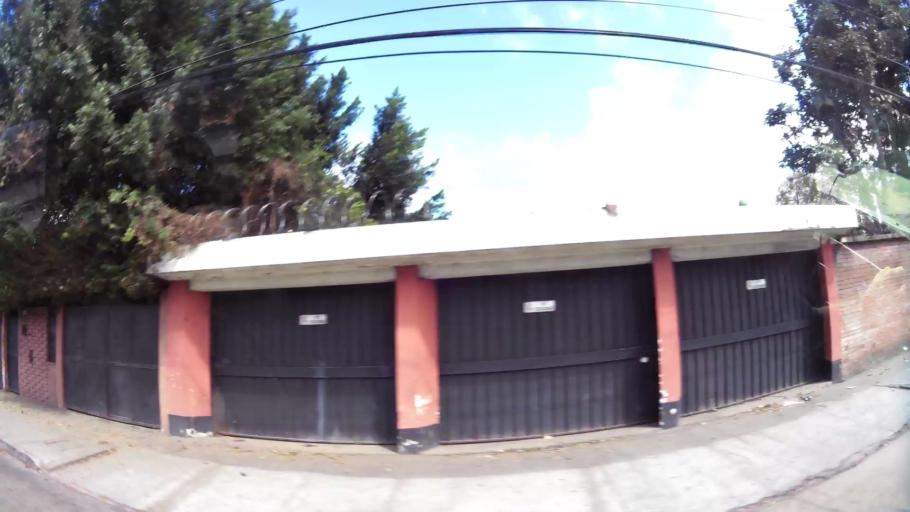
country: GT
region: Guatemala
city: Guatemala City
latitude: 14.6097
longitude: -90.5216
